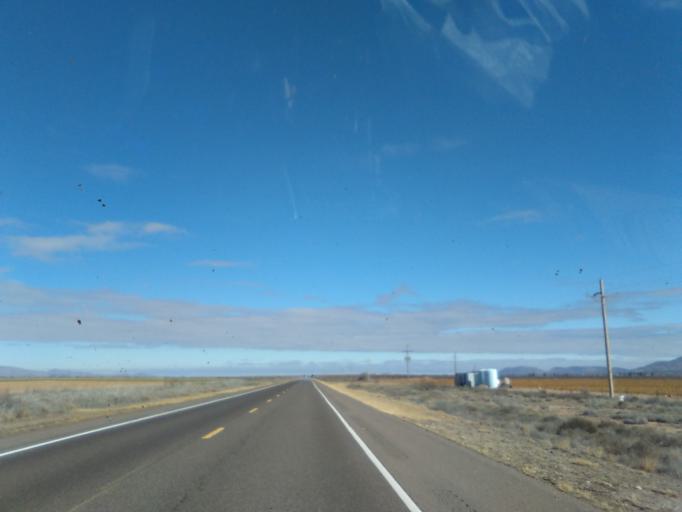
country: US
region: New Mexico
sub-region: Dona Ana County
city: Hatch
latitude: 32.6002
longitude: -107.3289
